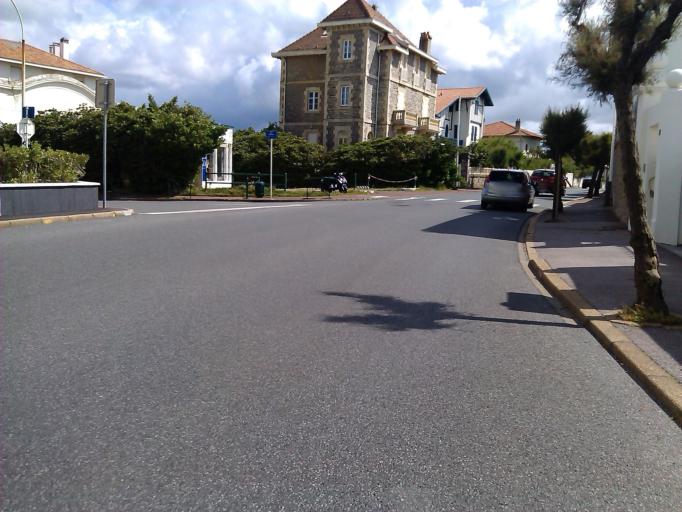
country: FR
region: Aquitaine
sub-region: Departement des Pyrenees-Atlantiques
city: Biarritz
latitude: 43.4910
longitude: -1.5520
